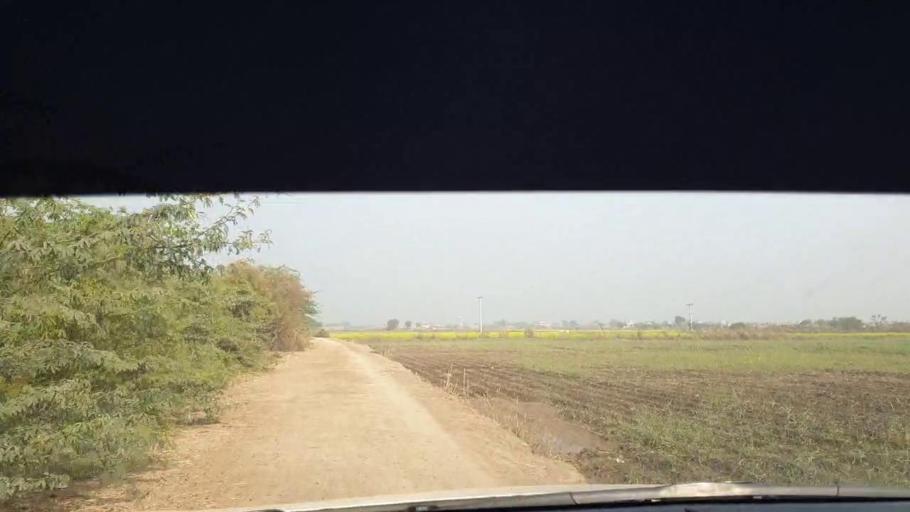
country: PK
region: Sindh
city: Berani
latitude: 25.7752
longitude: 68.8007
